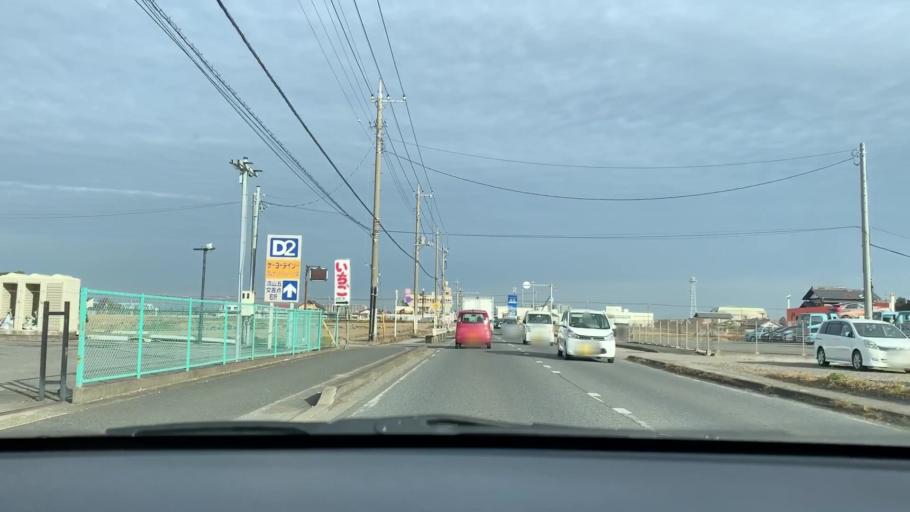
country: JP
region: Chiba
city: Nagareyama
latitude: 35.8216
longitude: 139.8955
